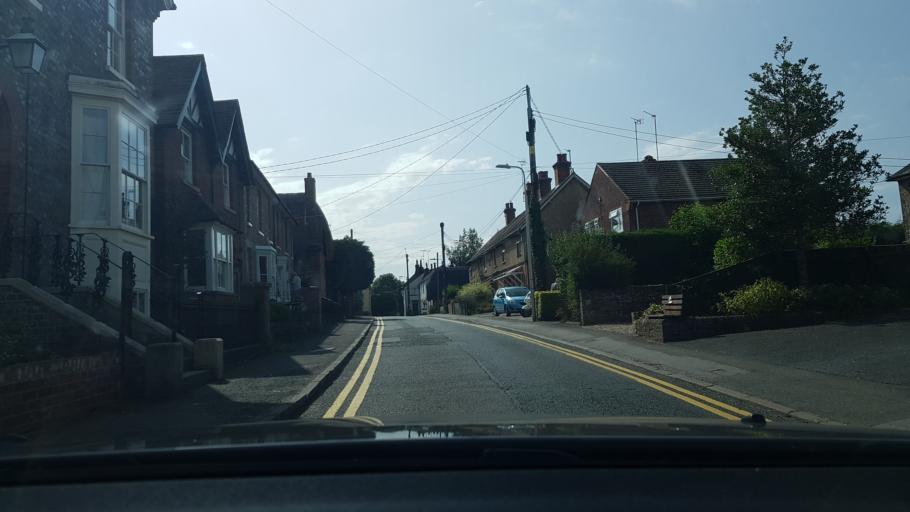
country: GB
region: England
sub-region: West Berkshire
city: Hungerford
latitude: 51.4148
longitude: -1.5187
